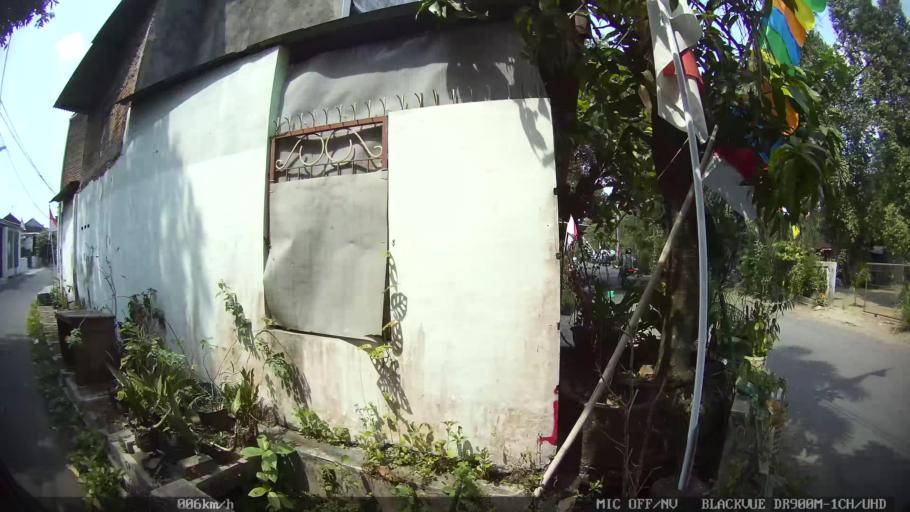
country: ID
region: Daerah Istimewa Yogyakarta
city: Yogyakarta
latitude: -7.8044
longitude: 110.3829
